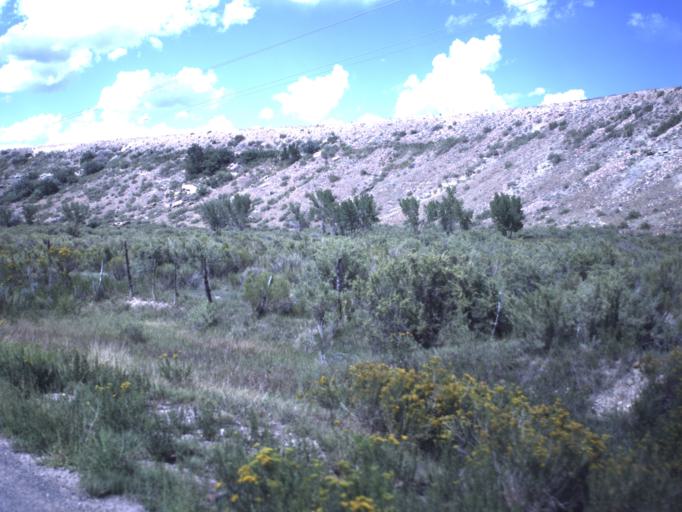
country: US
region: Utah
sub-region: Duchesne County
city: Duchesne
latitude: 40.1665
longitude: -110.4153
